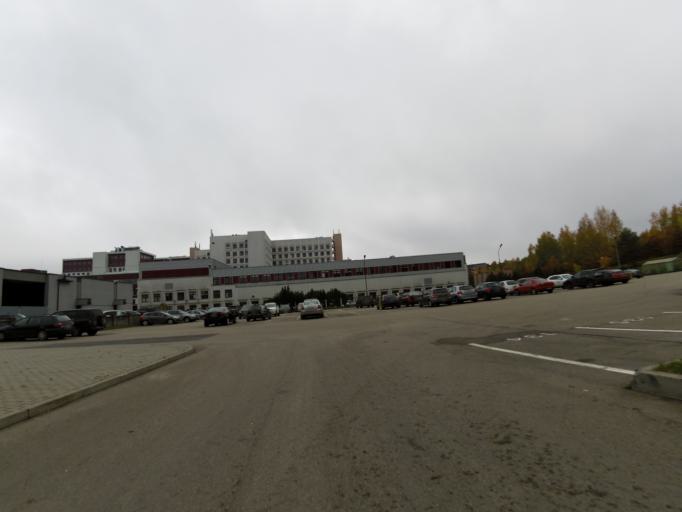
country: LT
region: Vilnius County
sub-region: Vilnius
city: Fabijoniskes
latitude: 54.7537
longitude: 25.2765
